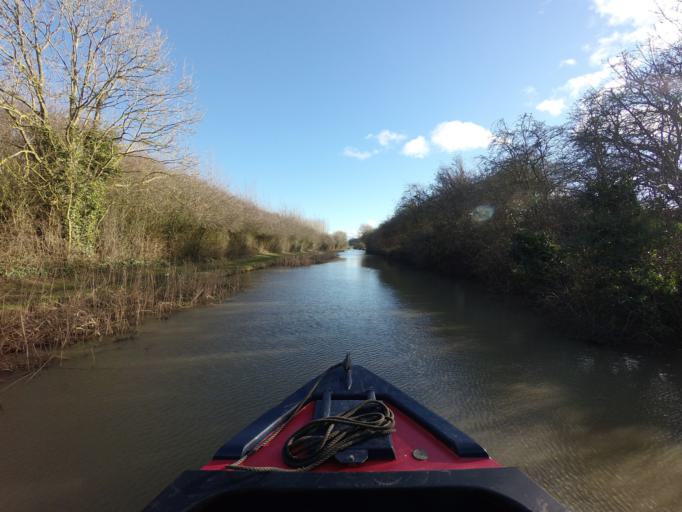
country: GB
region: England
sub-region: Northamptonshire
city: Blisworth
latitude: 52.1953
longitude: -0.9680
